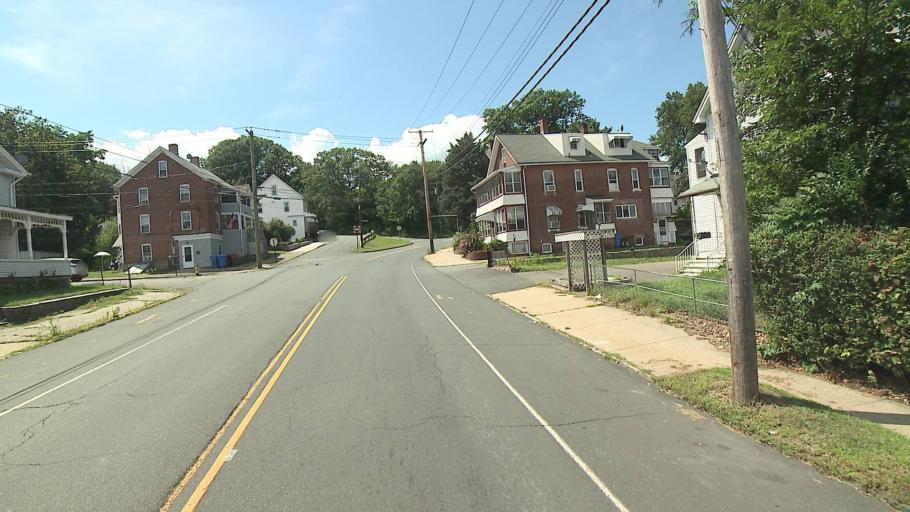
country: US
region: Connecticut
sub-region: Fairfield County
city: Shelton
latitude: 41.3190
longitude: -73.0996
